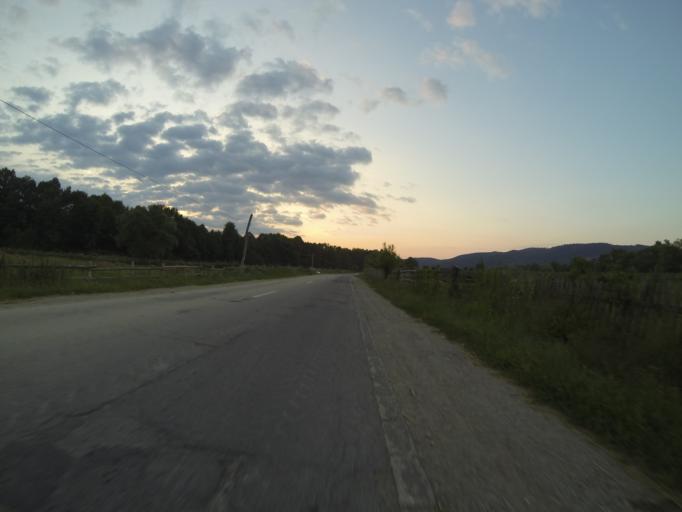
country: RO
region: Brasov
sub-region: Comuna Sinca Noua
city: Sinca Noua
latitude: 45.7108
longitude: 25.2433
